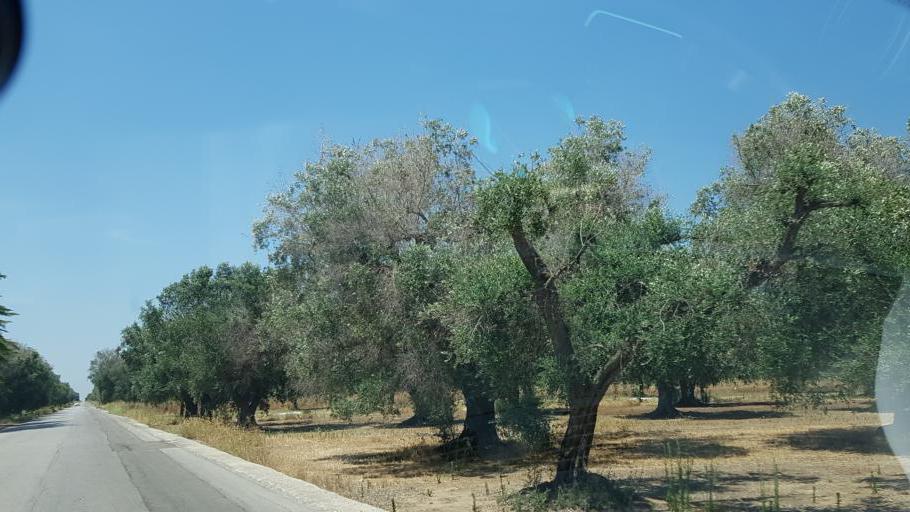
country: IT
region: Apulia
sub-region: Provincia di Brindisi
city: San Donaci
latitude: 40.4726
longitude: 17.8977
